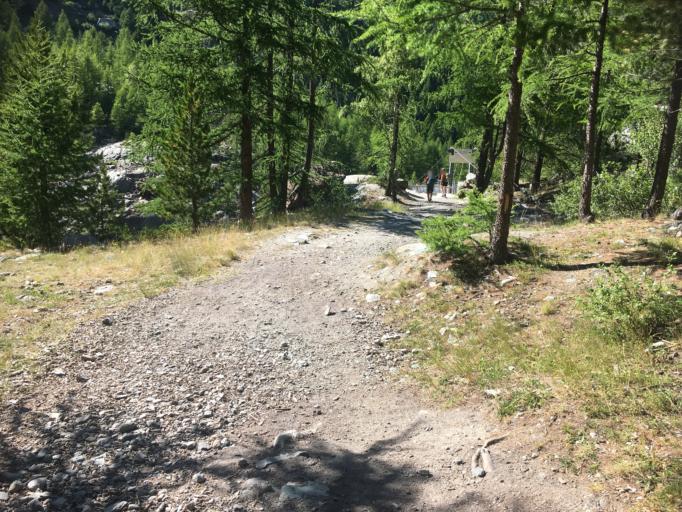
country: CH
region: Valais
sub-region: Visp District
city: Zermatt
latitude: 45.9961
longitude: 7.7286
